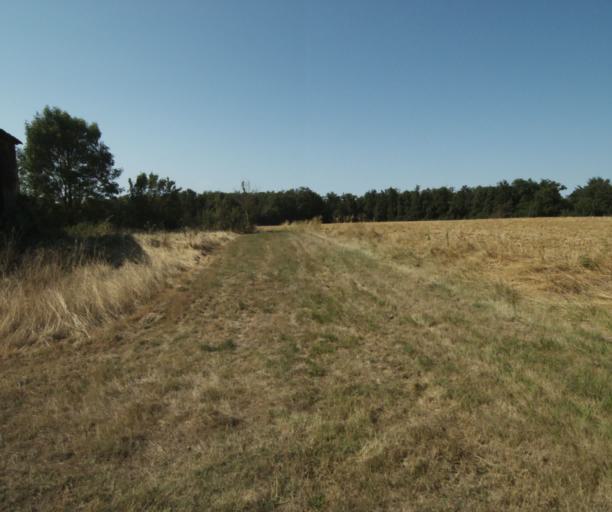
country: FR
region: Midi-Pyrenees
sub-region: Departement de la Haute-Garonne
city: Saint-Felix-Lauragais
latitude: 43.4285
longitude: 1.8416
